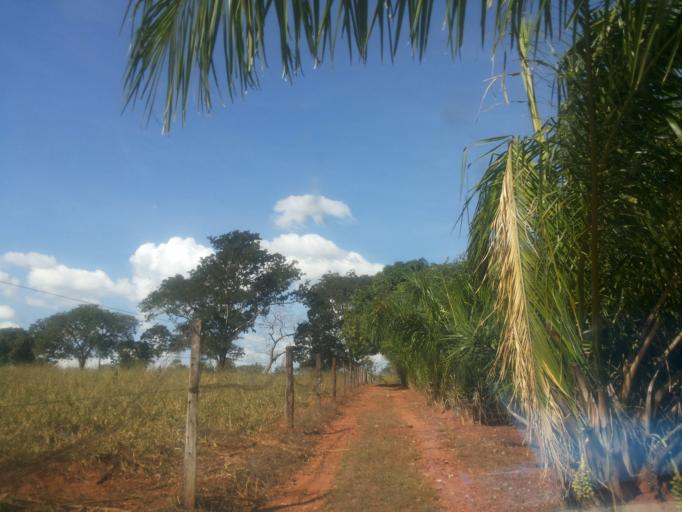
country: BR
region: Minas Gerais
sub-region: Santa Vitoria
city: Santa Vitoria
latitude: -18.9956
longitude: -50.3780
